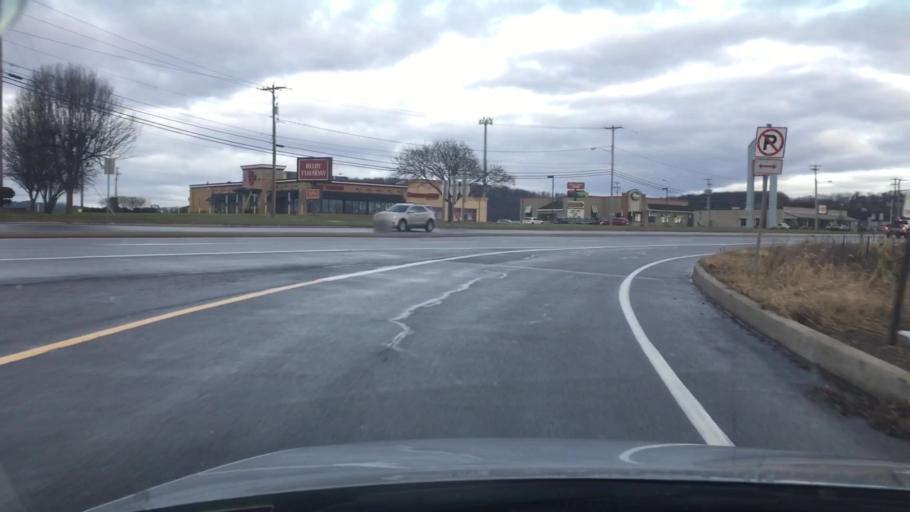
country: US
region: Pennsylvania
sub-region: Columbia County
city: Bloomsburg
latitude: 41.0156
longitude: -76.4910
